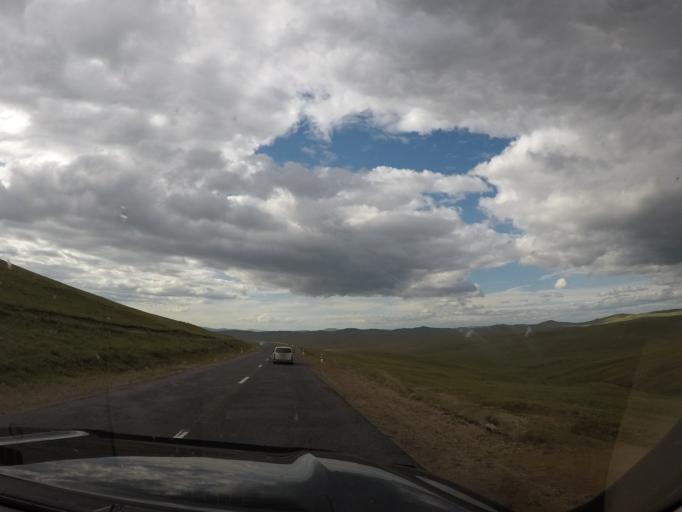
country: MN
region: Hentiy
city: Modot
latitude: 47.5868
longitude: 109.2908
